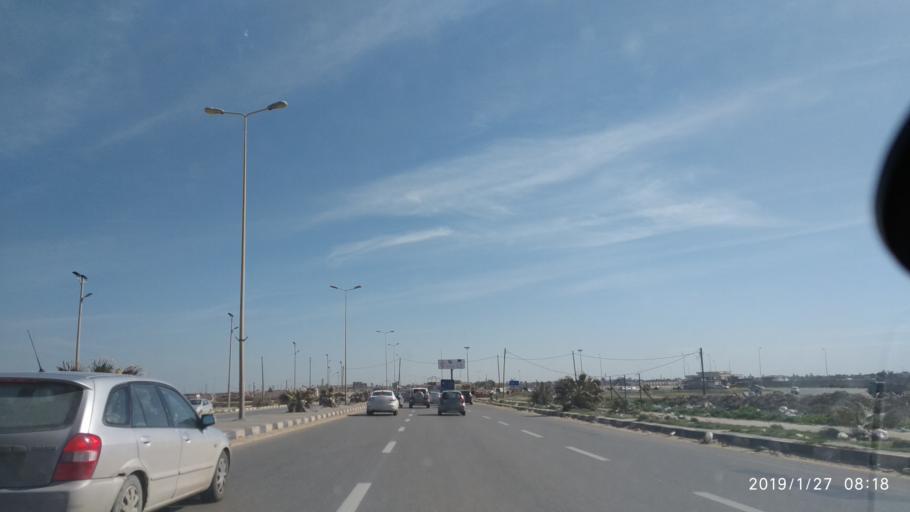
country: LY
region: Tripoli
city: Tagiura
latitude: 32.8969
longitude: 13.3201
